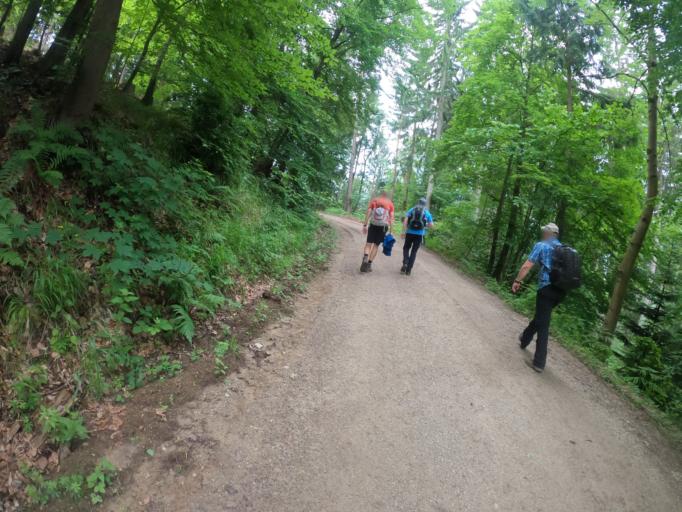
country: DE
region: Bavaria
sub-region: Upper Franconia
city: Litzendorf
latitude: 49.9266
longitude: 11.0296
